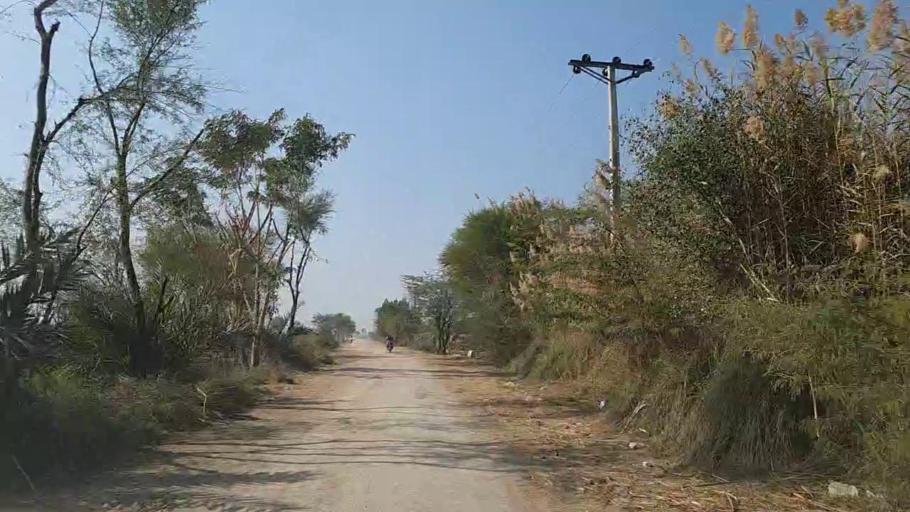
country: PK
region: Sindh
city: Daur
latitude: 26.5032
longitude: 68.3237
